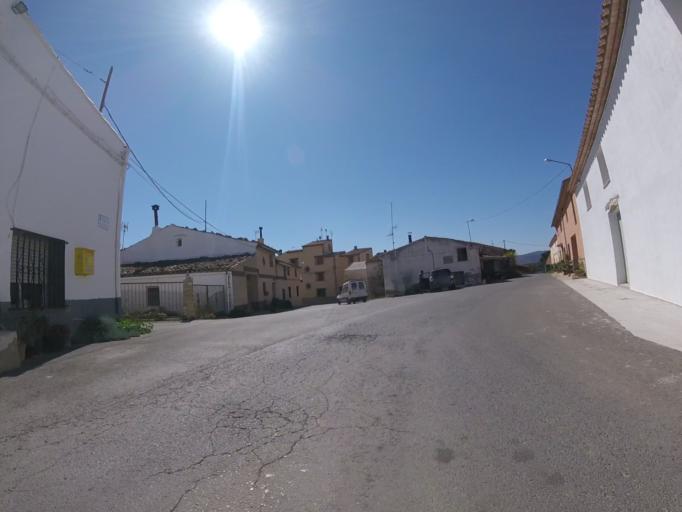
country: ES
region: Valencia
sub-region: Provincia de Castello
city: Cuevas de Vinroma
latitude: 40.3778
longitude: 0.1339
